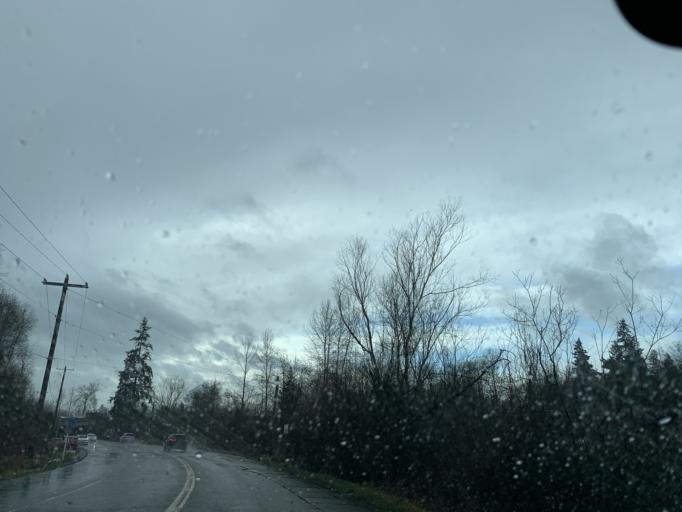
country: US
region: Washington
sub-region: Snohomish County
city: Alderwood Manor
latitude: 47.8403
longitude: -122.2707
